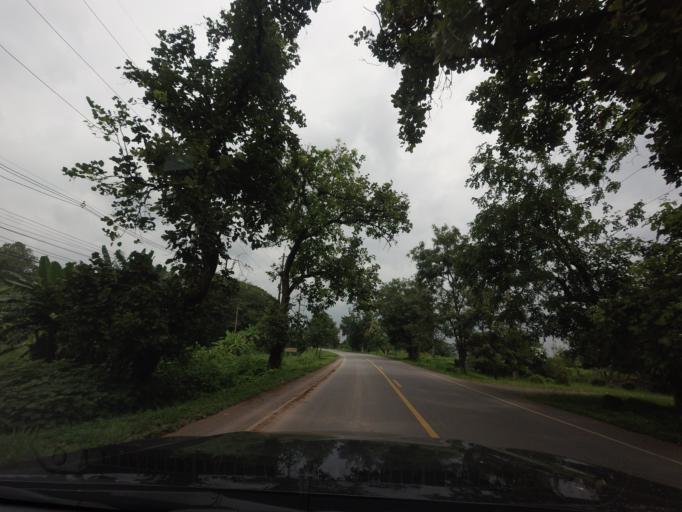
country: TH
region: Nong Khai
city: Si Chiang Mai
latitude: 17.9383
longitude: 102.6090
